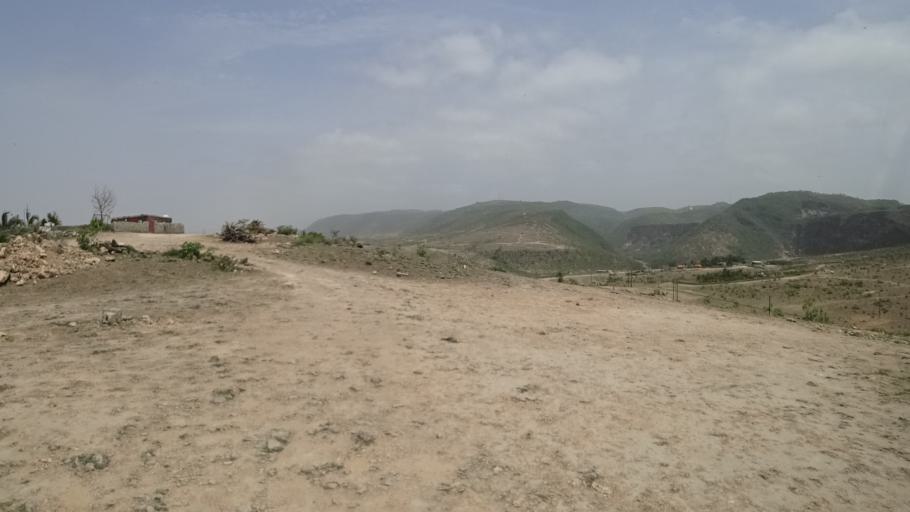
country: OM
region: Zufar
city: Salalah
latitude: 17.0664
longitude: 54.4361
